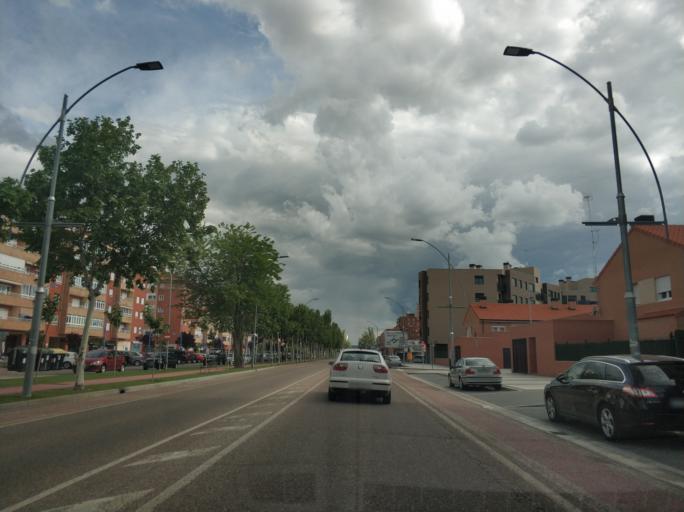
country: ES
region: Castille and Leon
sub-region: Provincia de Burgos
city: Aranda de Duero
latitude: 41.6644
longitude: -3.6914
